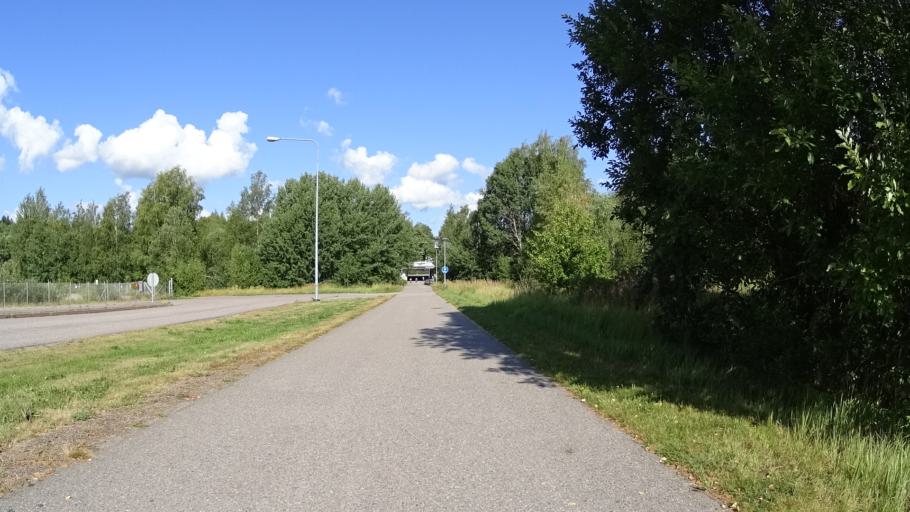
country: FI
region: Uusimaa
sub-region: Helsinki
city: Espoo
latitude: 60.1875
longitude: 24.6015
